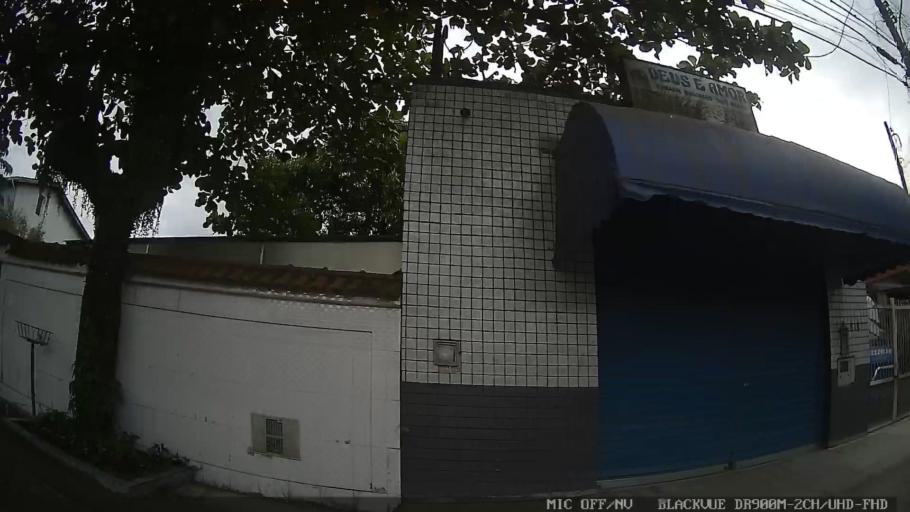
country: BR
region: Sao Paulo
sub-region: Guaruja
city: Guaruja
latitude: -23.9964
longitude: -46.2796
